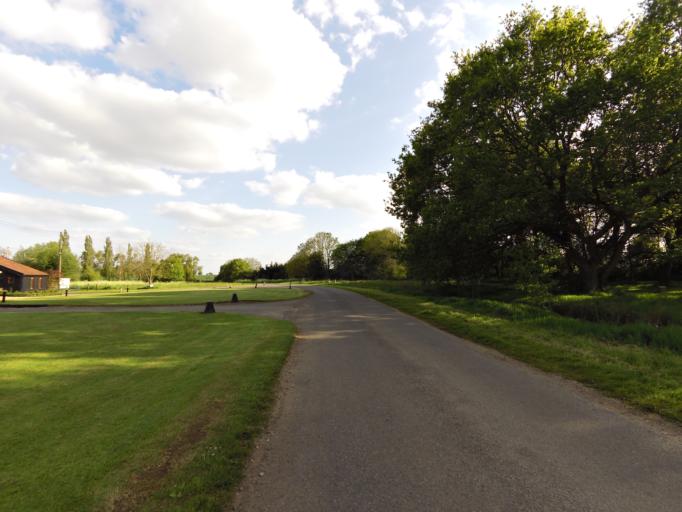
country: GB
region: England
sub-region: Suffolk
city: Halesworth
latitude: 52.4048
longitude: 1.5071
